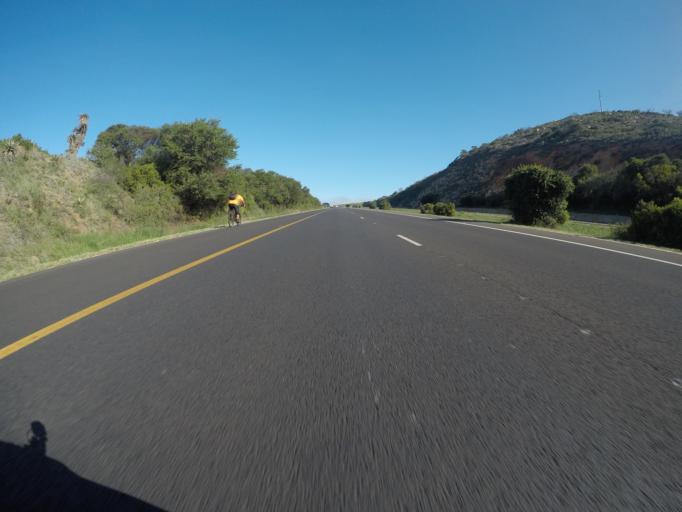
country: ZA
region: Western Cape
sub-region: Eden District Municipality
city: Mossel Bay
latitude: -34.1538
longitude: 22.0993
